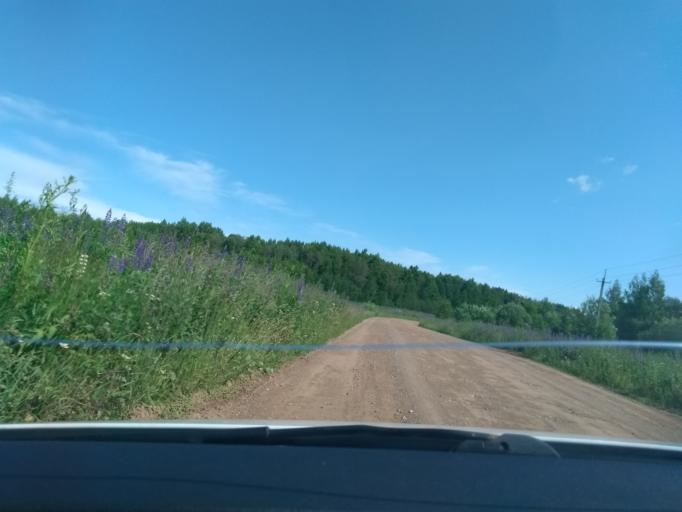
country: RU
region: Perm
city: Sylva
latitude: 57.8254
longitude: 56.7475
